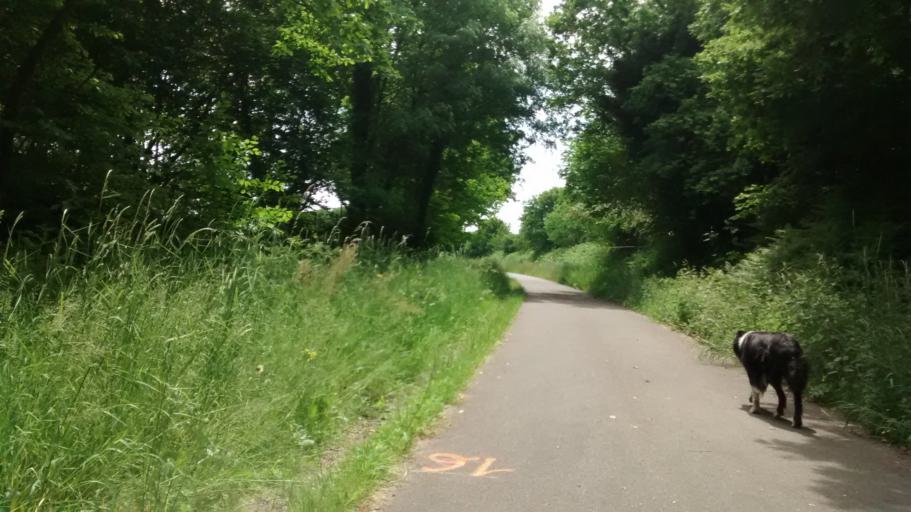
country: FR
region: Brittany
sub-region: Departement du Morbihan
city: Molac
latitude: 47.7005
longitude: -2.4352
